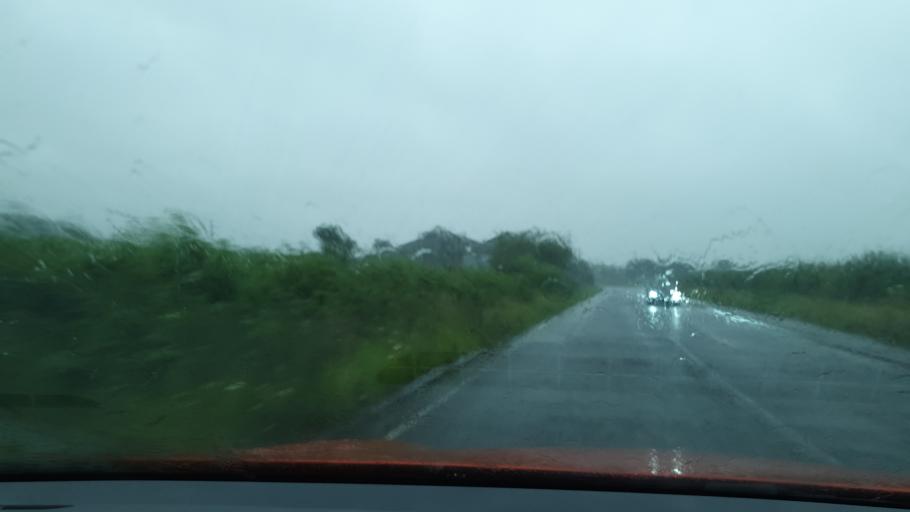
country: GB
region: England
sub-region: Cumbria
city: Millom
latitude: 54.2648
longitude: -3.2151
